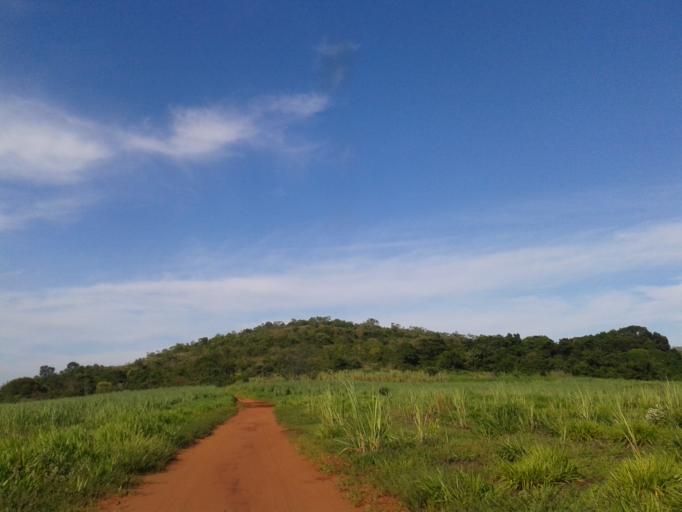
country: BR
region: Minas Gerais
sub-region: Santa Vitoria
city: Santa Vitoria
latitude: -19.1179
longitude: -49.9937
